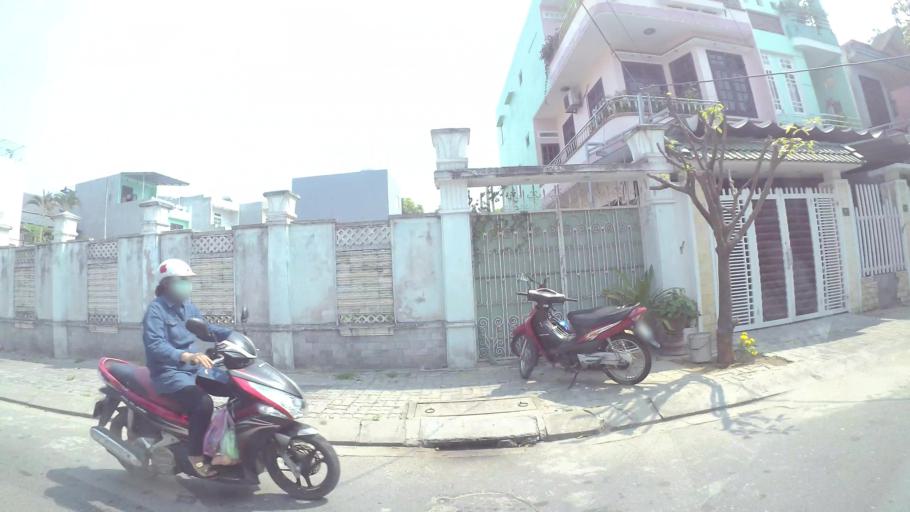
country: VN
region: Da Nang
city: Son Tra
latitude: 16.0407
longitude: 108.2453
